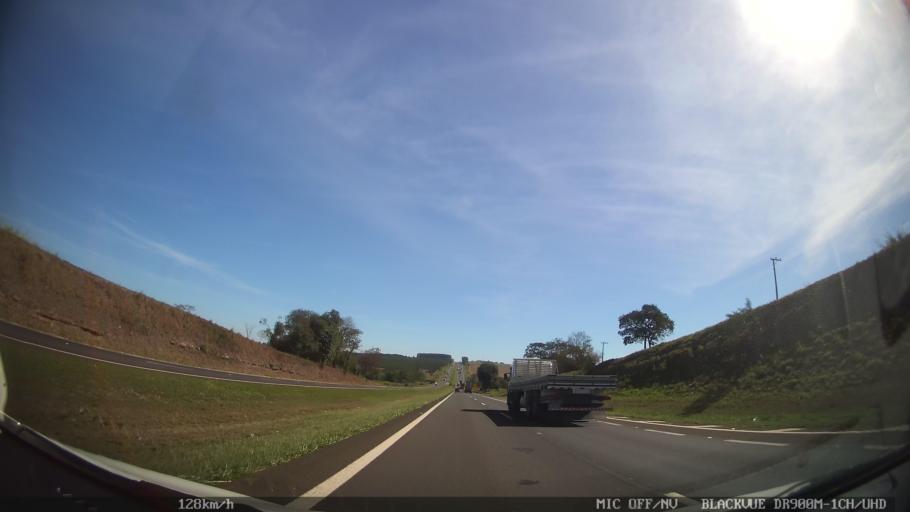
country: BR
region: Sao Paulo
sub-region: Porto Ferreira
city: Porto Ferreira
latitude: -21.7937
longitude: -47.5156
